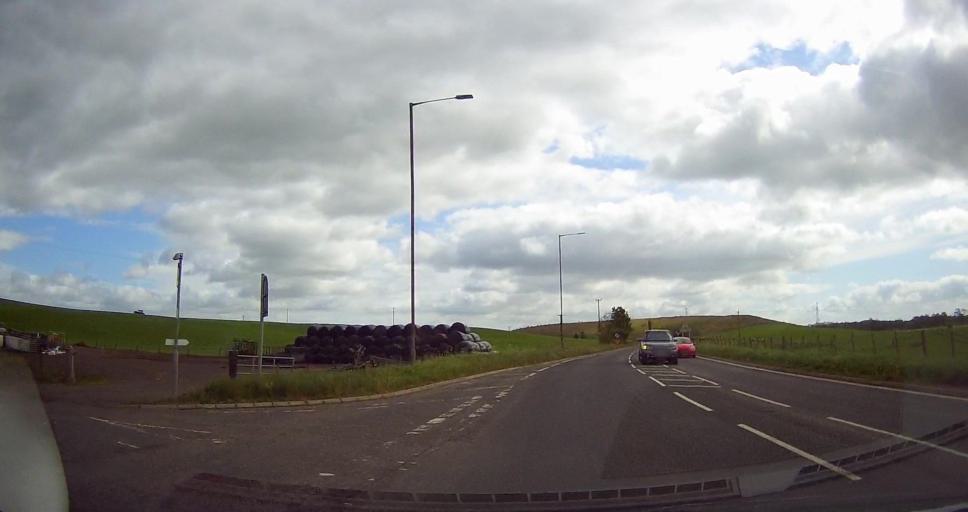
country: GB
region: Scotland
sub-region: Clackmannanshire
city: Dollar
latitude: 56.1267
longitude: -3.6847
